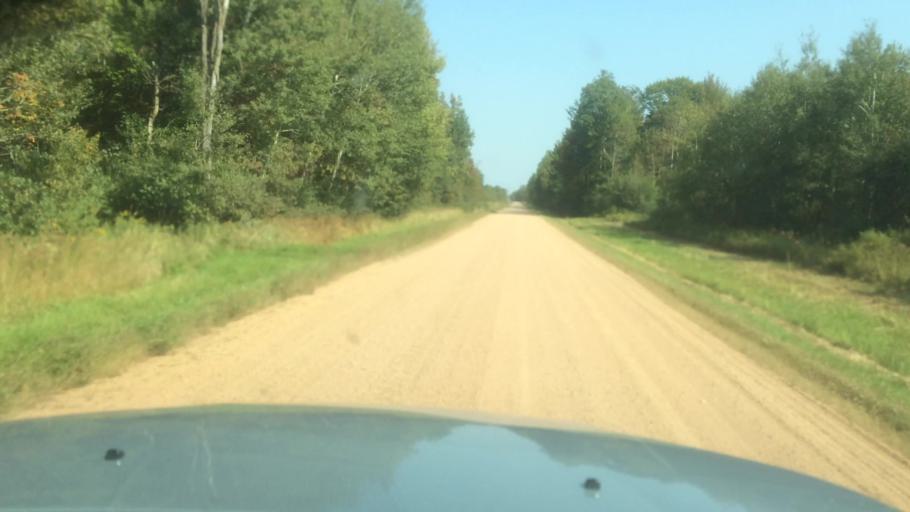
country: US
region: Wisconsin
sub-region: Taylor County
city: Medford
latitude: 45.0914
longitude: -90.2911
